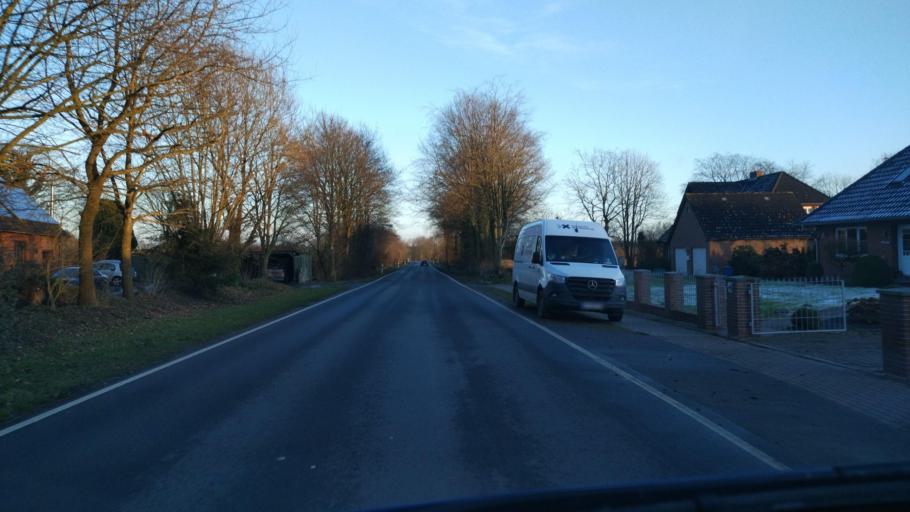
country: DE
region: Schleswig-Holstein
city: Ostenfeld
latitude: 54.4607
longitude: 9.2470
